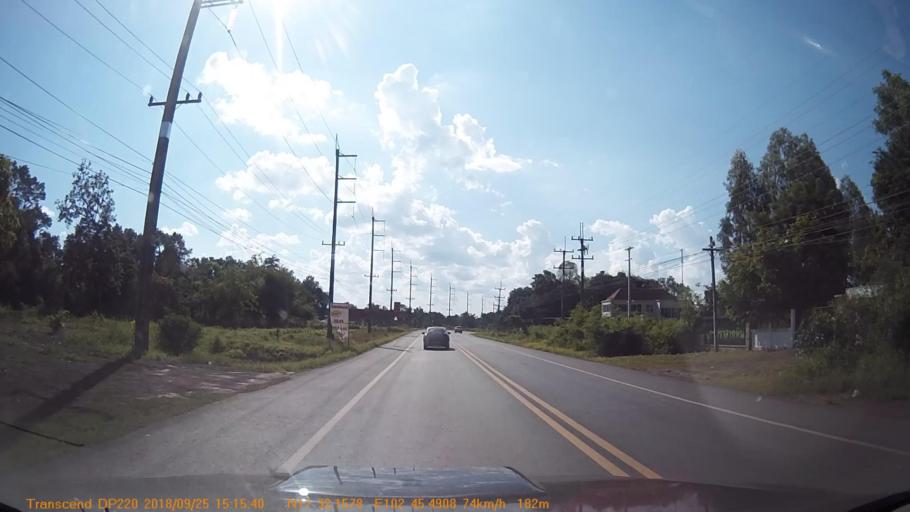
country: TH
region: Changwat Udon Thani
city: Udon Thani
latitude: 17.5360
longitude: 102.7578
